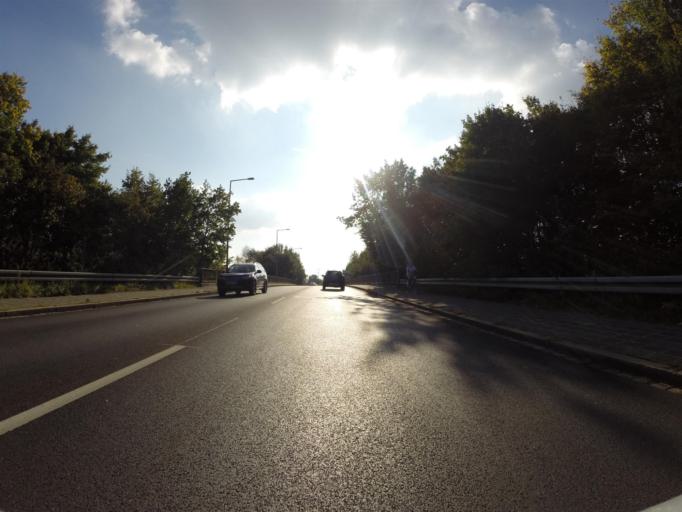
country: DE
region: Bavaria
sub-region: Regierungsbezirk Mittelfranken
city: Grossreuth bei Schweinau
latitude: 49.4330
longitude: 11.0212
